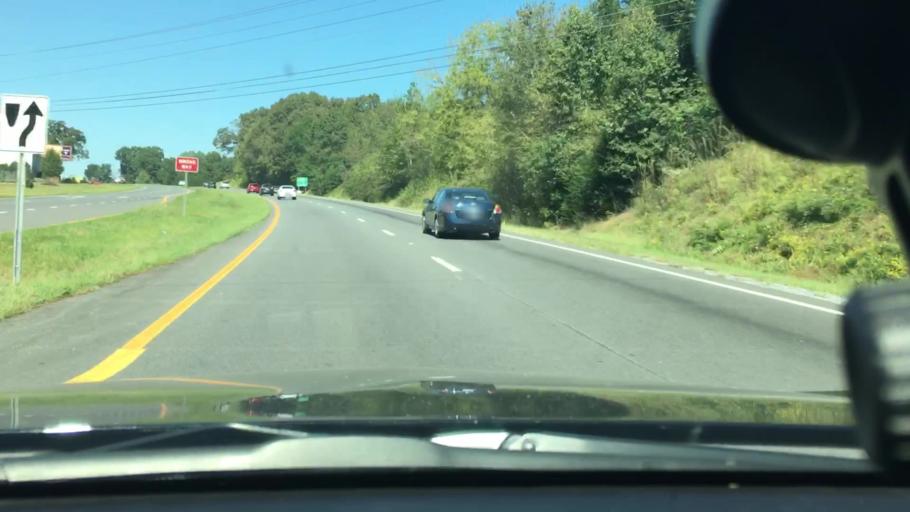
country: US
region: North Carolina
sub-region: Cleveland County
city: White Plains
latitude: 35.2593
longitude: -81.4607
